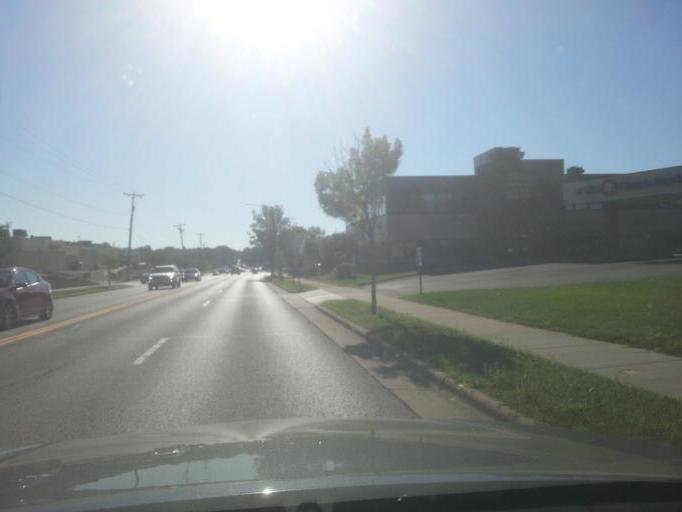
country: US
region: Wisconsin
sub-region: Dane County
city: Shorewood Hills
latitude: 43.0500
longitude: -89.4764
